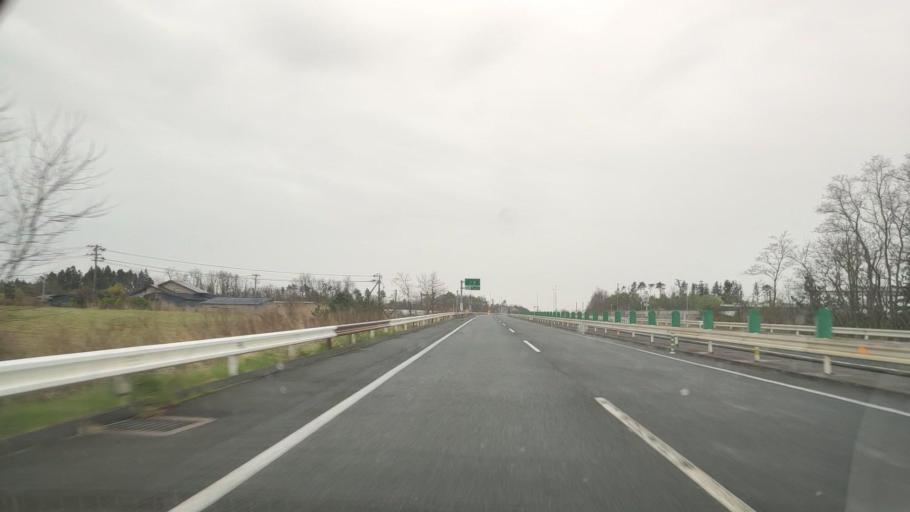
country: JP
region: Akita
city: Noshiromachi
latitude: 40.1235
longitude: 140.0122
